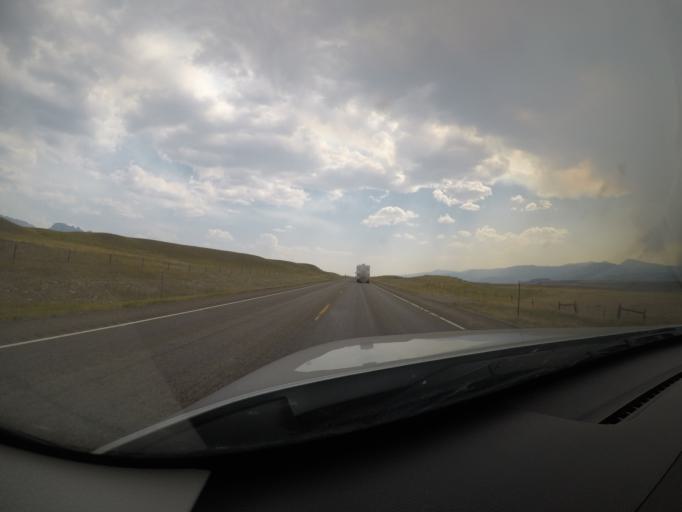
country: US
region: Montana
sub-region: Gallatin County
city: Big Sky
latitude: 45.0943
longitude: -111.6484
